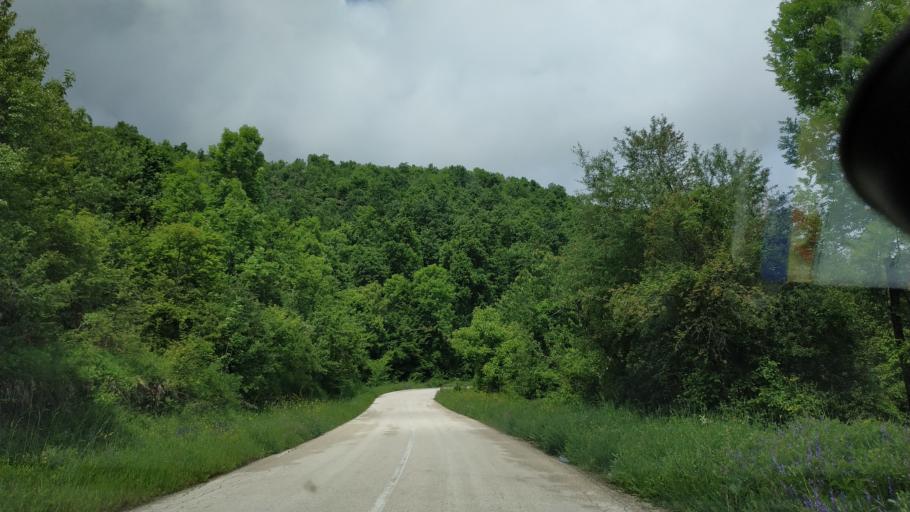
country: RS
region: Central Serbia
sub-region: Zajecarski Okrug
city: Boljevac
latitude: 43.7364
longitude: 21.9517
